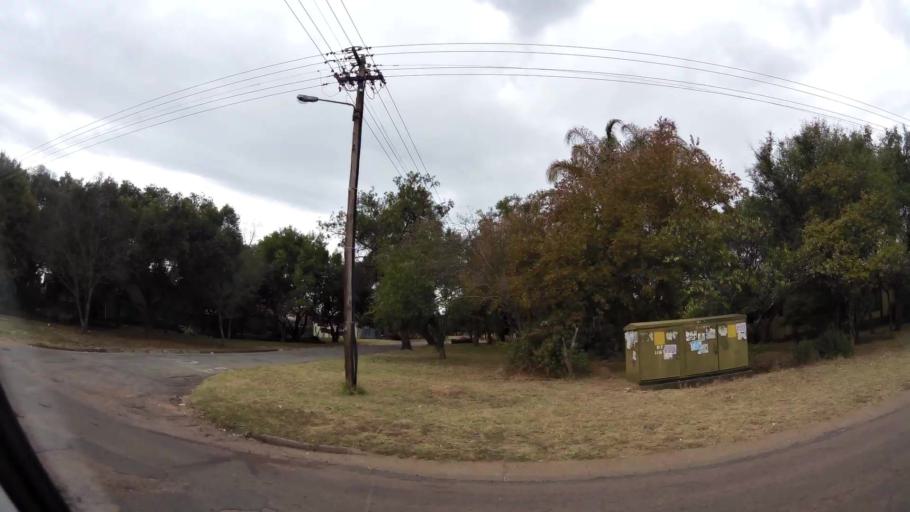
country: ZA
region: Limpopo
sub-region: Waterberg District Municipality
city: Modimolle
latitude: -24.6997
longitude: 28.4142
